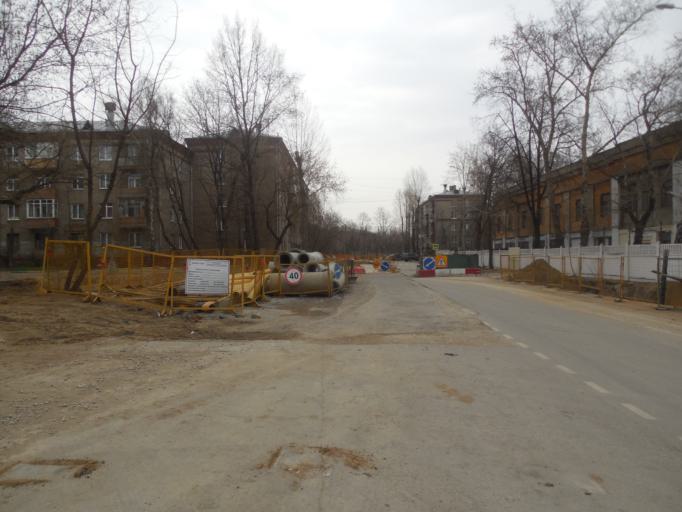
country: RU
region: Moscow
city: Ryazanskiy
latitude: 55.7615
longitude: 37.7394
